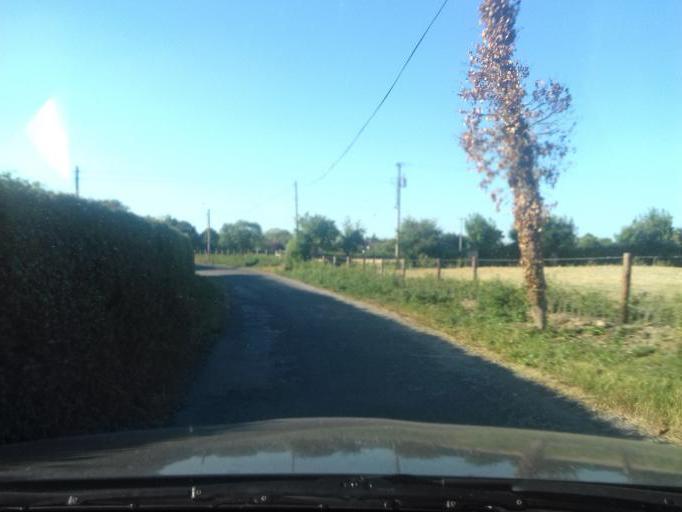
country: IE
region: Leinster
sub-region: An Mhi
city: Ashbourne
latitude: 53.4520
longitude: -6.3794
